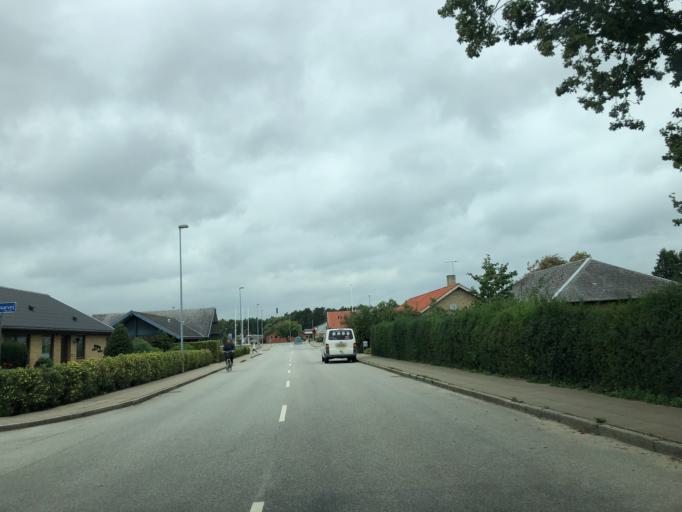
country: DK
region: Central Jutland
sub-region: Herning Kommune
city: Snejbjerg
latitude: 56.1310
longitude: 8.8999
